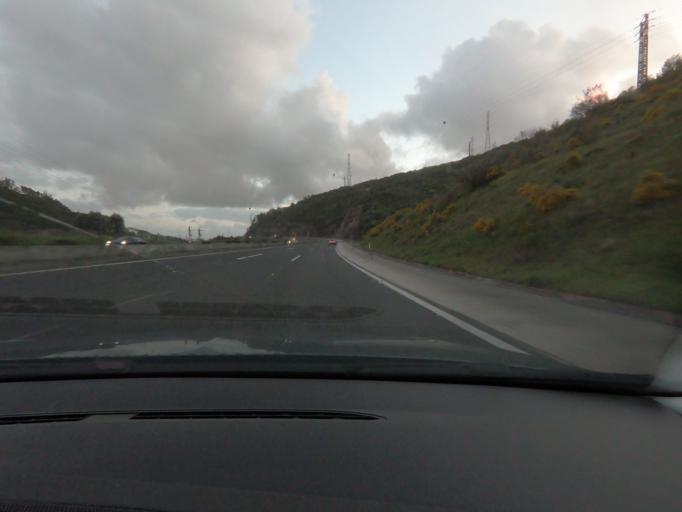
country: PT
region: Lisbon
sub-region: Loures
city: Bucelas
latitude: 38.8869
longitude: -9.1278
